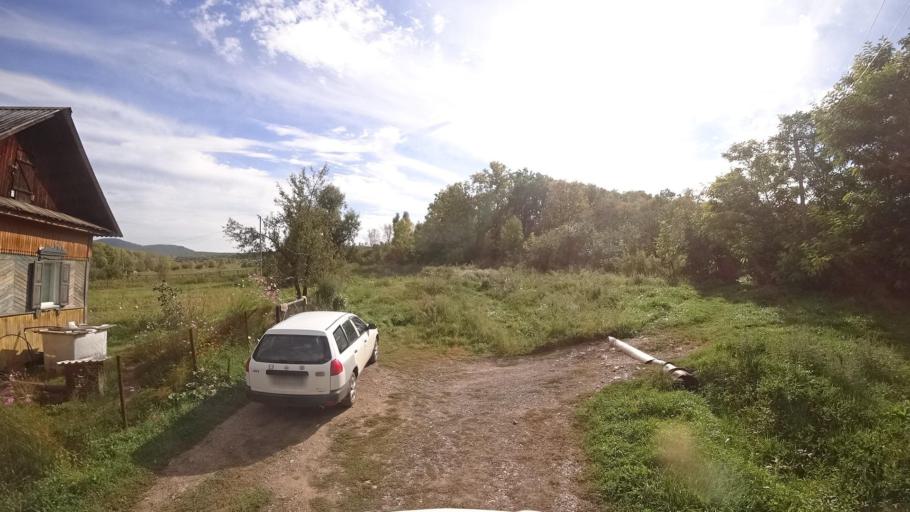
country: RU
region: Primorskiy
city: Dostoyevka
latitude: 44.2928
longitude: 133.4581
